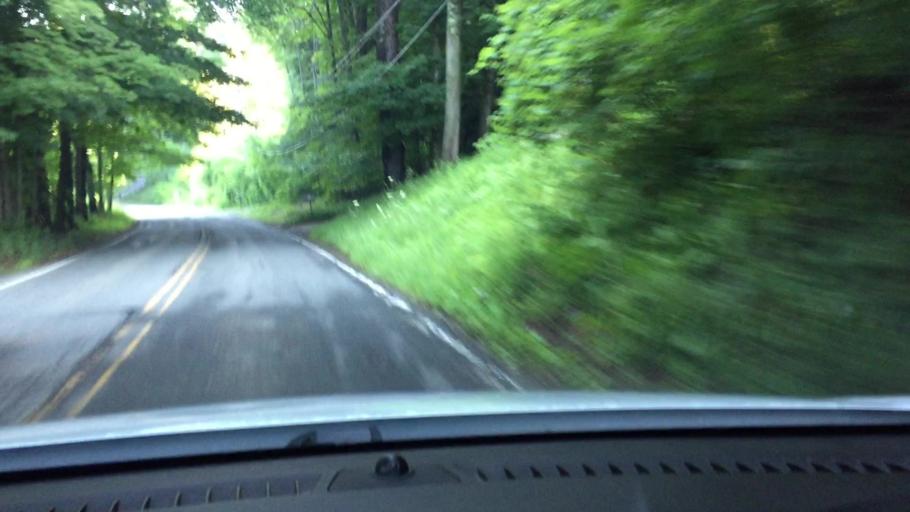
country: US
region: Massachusetts
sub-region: Berkshire County
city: Pittsfield
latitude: 42.4047
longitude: -73.2319
